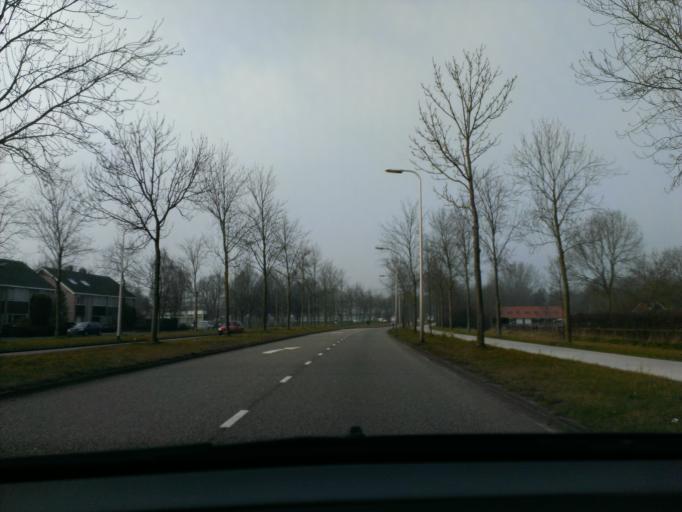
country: NL
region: Overijssel
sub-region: Gemeente Zwolle
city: Zwolle
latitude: 52.5255
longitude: 6.0941
